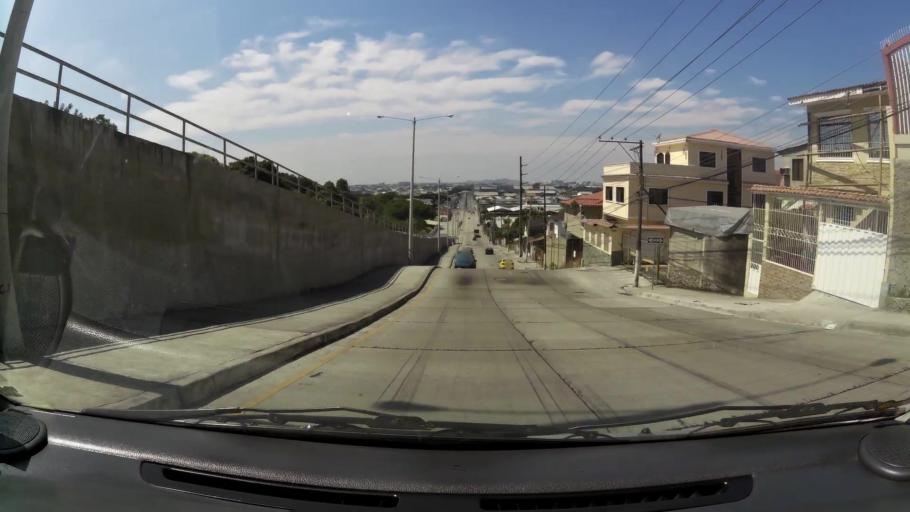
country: EC
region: Guayas
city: Guayaquil
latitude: -2.1354
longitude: -79.9188
